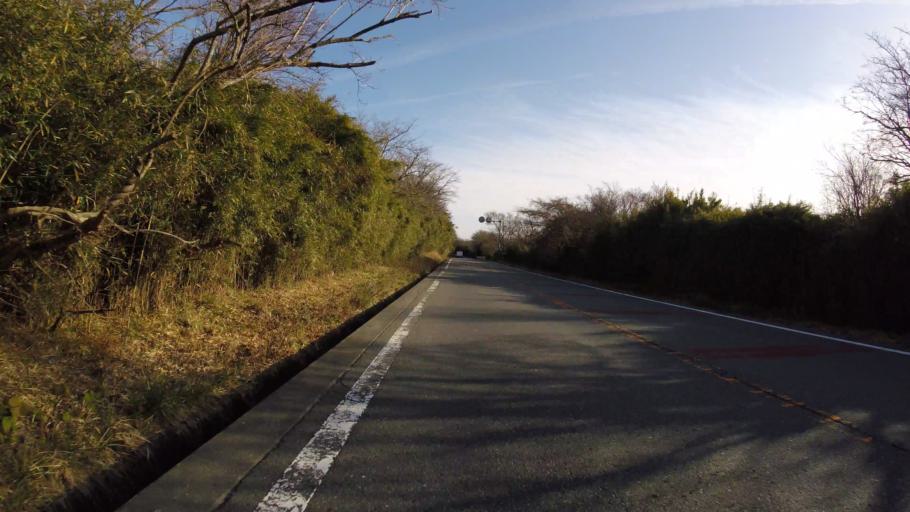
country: JP
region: Kanagawa
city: Hakone
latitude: 35.1501
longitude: 139.0256
